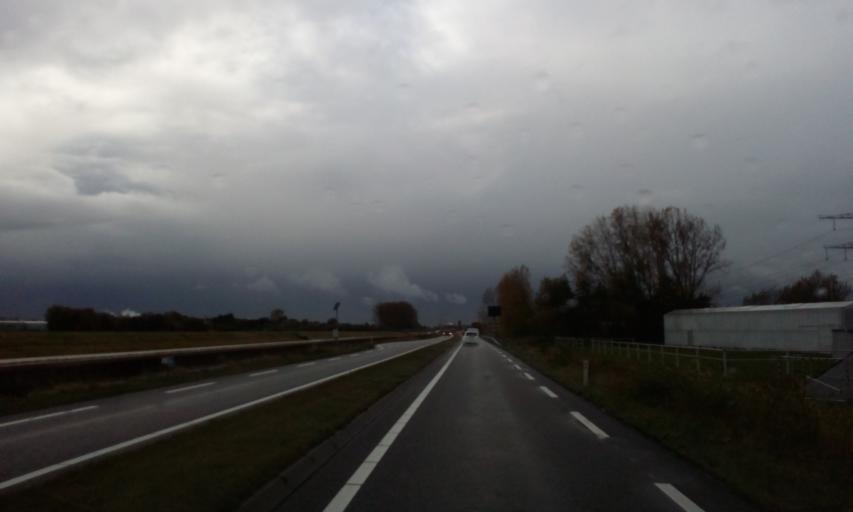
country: NL
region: South Holland
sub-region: Gemeente Westland
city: Kwintsheul
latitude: 51.9979
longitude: 4.2692
